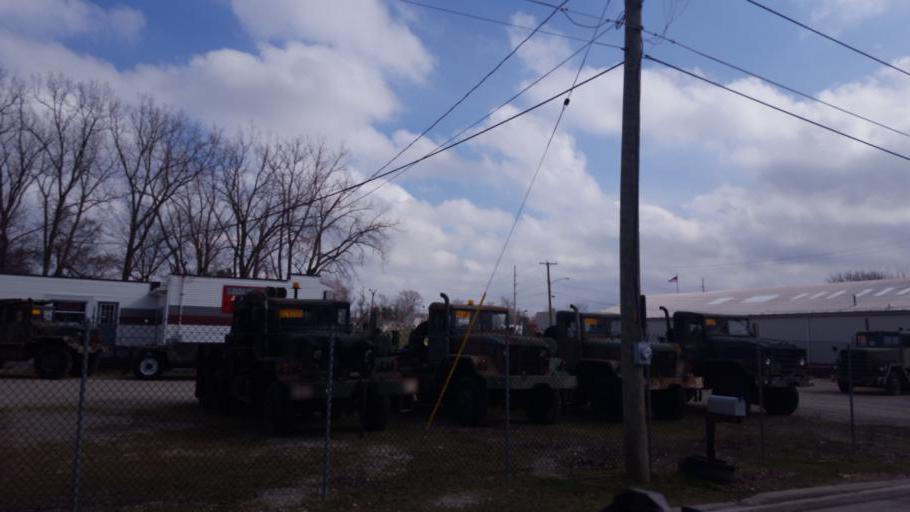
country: US
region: Ohio
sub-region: Richland County
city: Shelby
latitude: 40.8845
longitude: -82.6591
